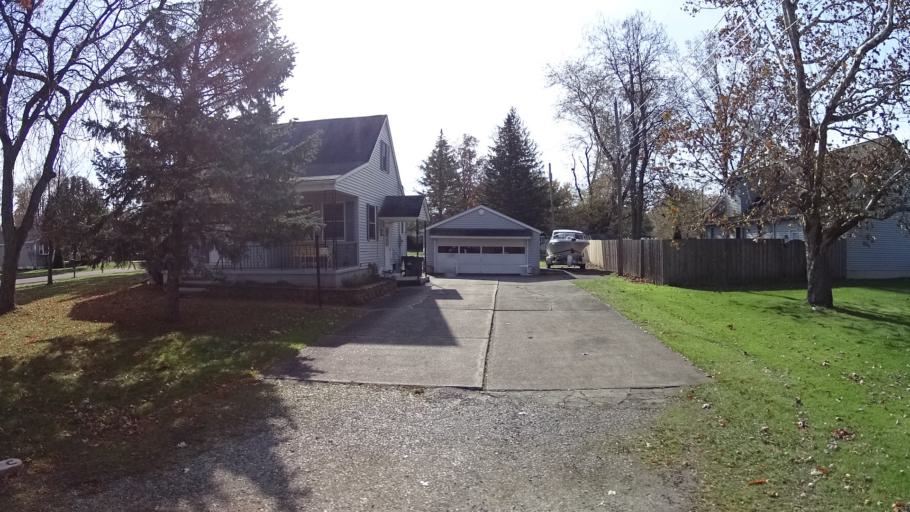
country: US
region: Ohio
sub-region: Lorain County
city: Sheffield Lake
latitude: 41.4876
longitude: -82.1045
